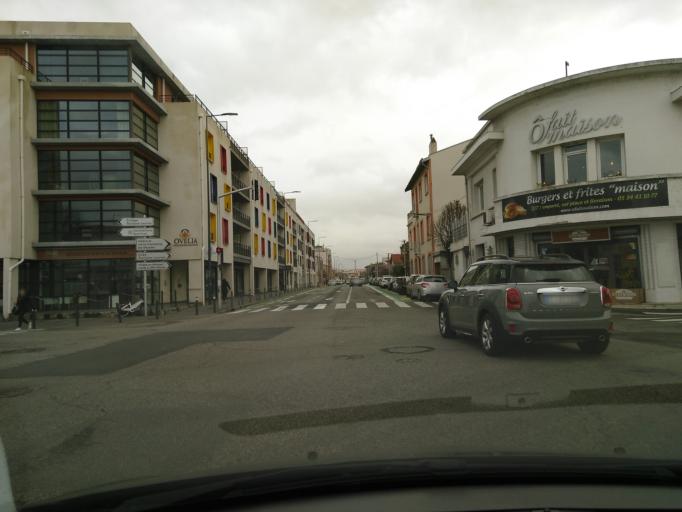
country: FR
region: Midi-Pyrenees
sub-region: Departement de la Haute-Garonne
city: Toulouse
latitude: 43.6262
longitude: 1.4370
